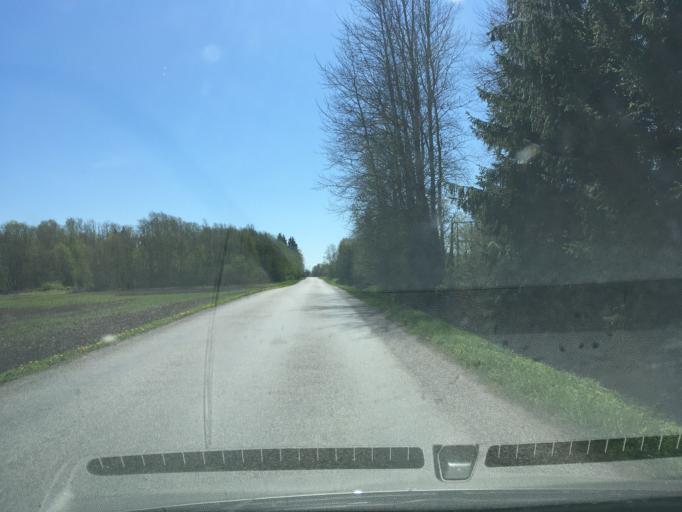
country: EE
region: Harju
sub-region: Raasiku vald
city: Arukula
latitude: 59.4096
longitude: 25.0768
